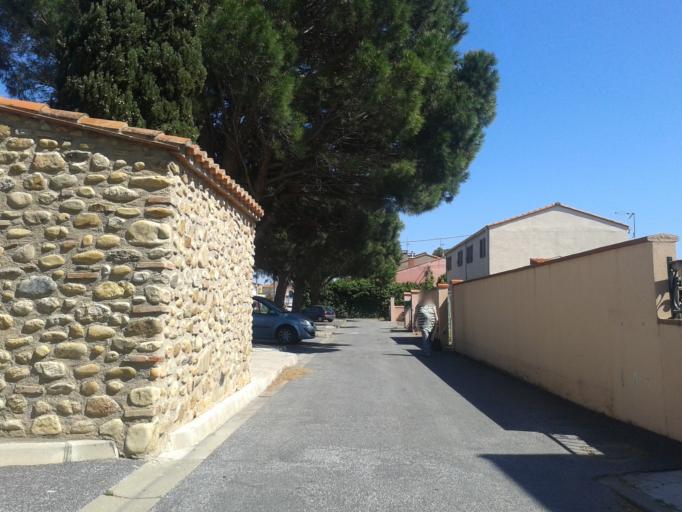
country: FR
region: Languedoc-Roussillon
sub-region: Departement des Pyrenees-Orientales
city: Millas
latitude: 42.6923
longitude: 2.6894
